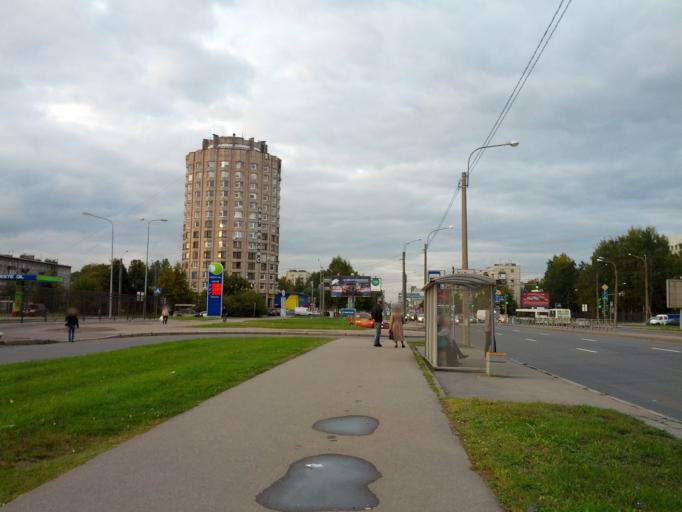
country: RU
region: St.-Petersburg
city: Krasnogvargeisky
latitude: 59.9521
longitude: 30.4366
